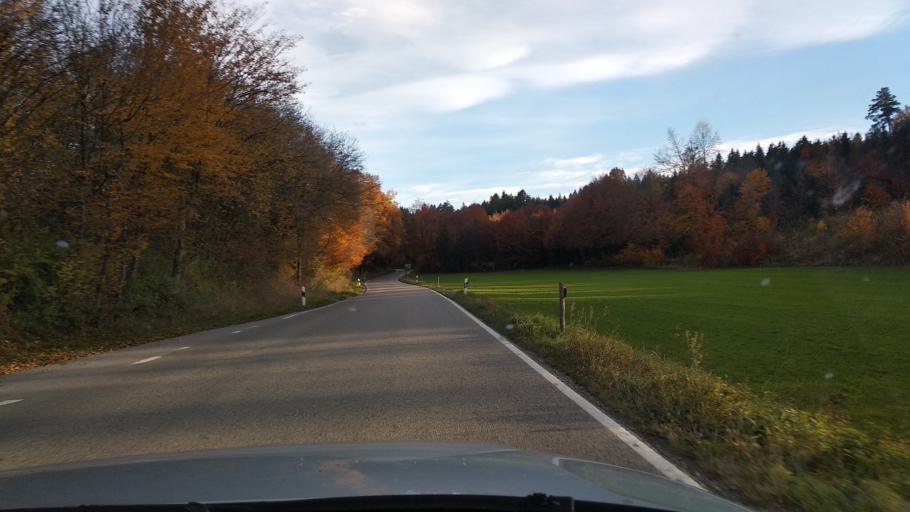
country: DE
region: Bavaria
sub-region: Upper Bavaria
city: Moosach
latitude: 48.0561
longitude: 11.8533
